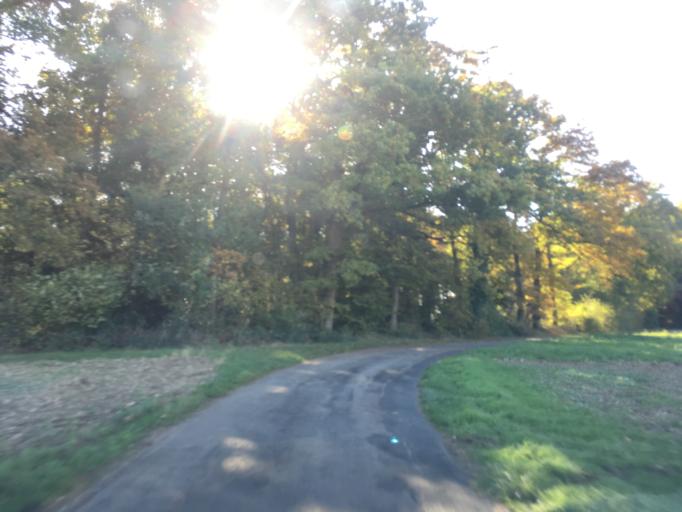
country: FR
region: Haute-Normandie
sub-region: Departement de l'Eure
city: Heudreville-sur-Eure
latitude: 49.1411
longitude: 1.2164
